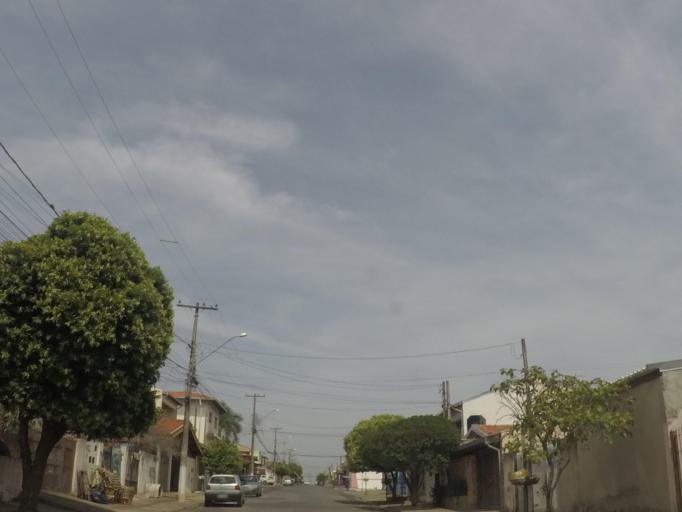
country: BR
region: Sao Paulo
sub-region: Hortolandia
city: Hortolandia
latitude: -22.8509
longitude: -47.1870
